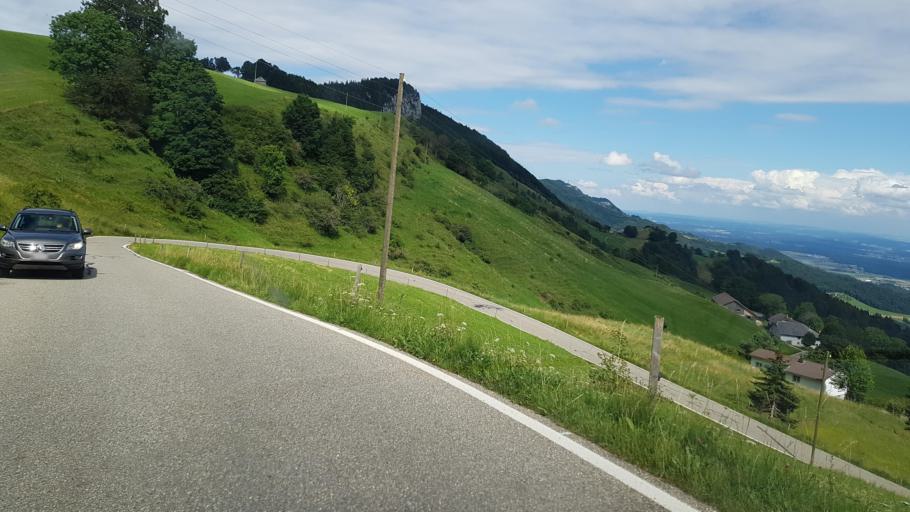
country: CH
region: Solothurn
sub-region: Bezirk Thal
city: Welschenrohr
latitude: 47.2625
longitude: 7.5393
